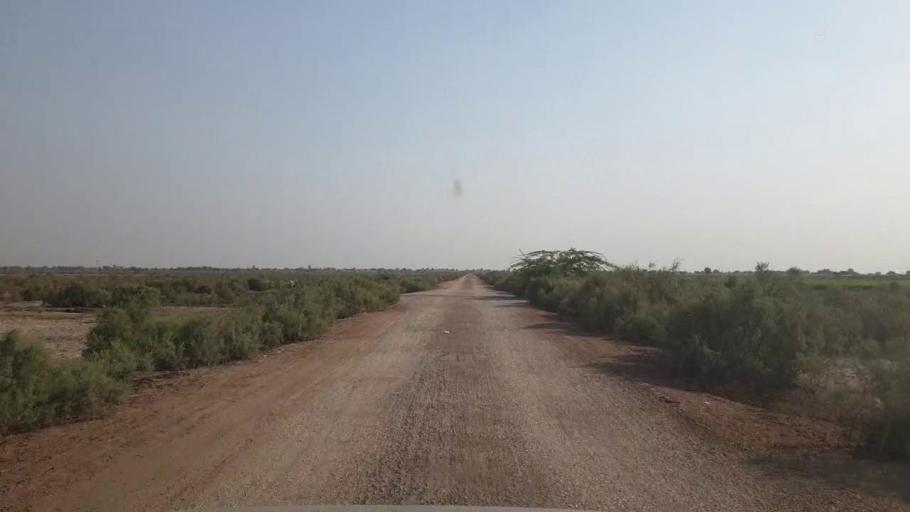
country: PK
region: Sindh
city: Sanghar
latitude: 26.0549
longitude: 68.8967
